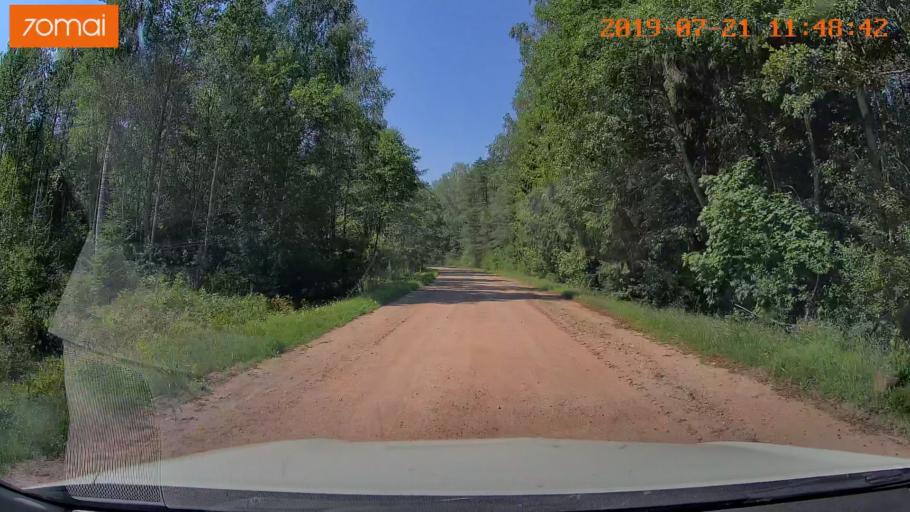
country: BY
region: Grodnenskaya
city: Lyubcha
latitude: 53.8964
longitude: 26.0471
